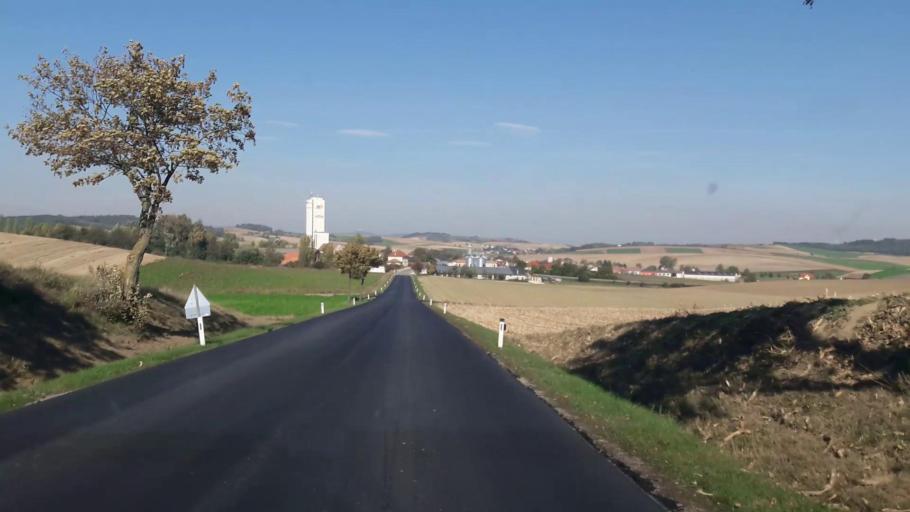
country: AT
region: Lower Austria
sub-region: Politischer Bezirk Korneuburg
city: Grossrussbach
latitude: 48.4695
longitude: 16.3794
